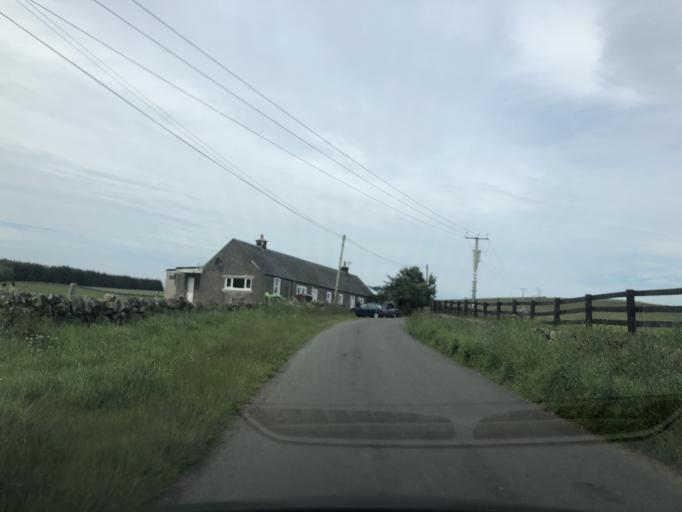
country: GB
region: Scotland
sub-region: The Scottish Borders
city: West Linton
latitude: 55.7634
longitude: -3.3280
